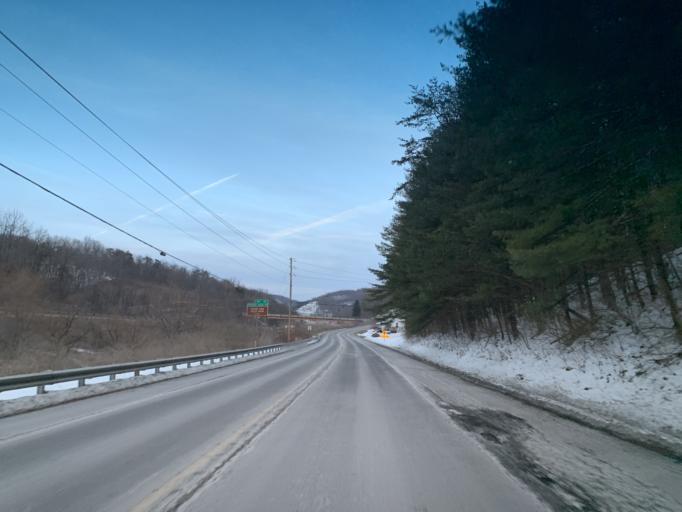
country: US
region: Maryland
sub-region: Allegany County
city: Cumberland
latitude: 39.6811
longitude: -78.6723
